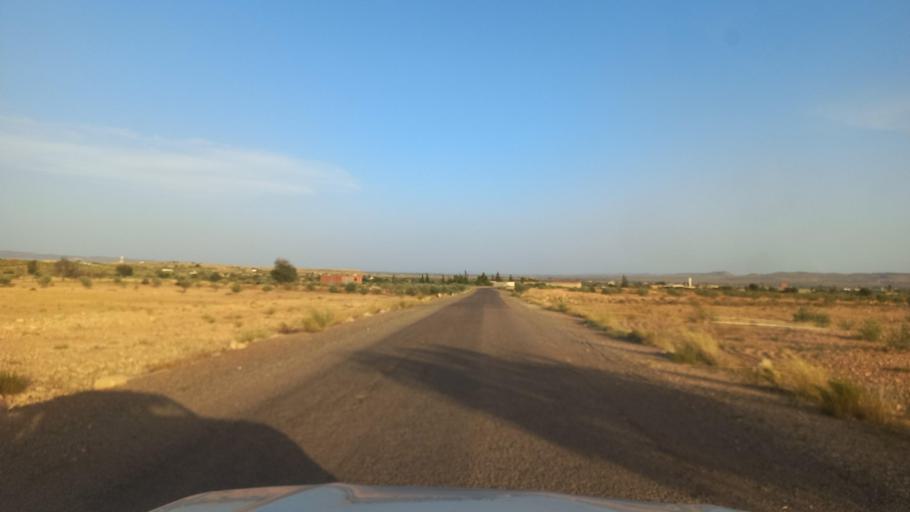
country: TN
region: Al Qasrayn
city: Kasserine
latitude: 35.2725
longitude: 8.9257
